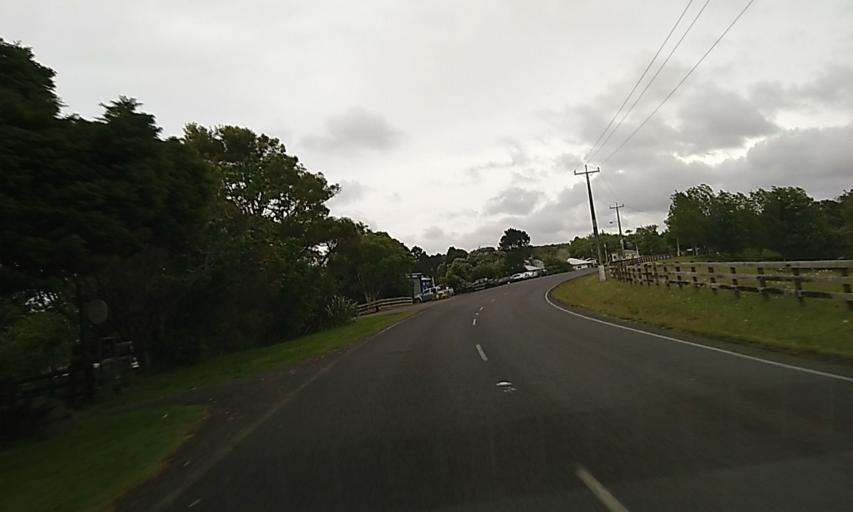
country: NZ
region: Auckland
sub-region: Auckland
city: Pukekohe East
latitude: -37.3247
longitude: 174.9178
